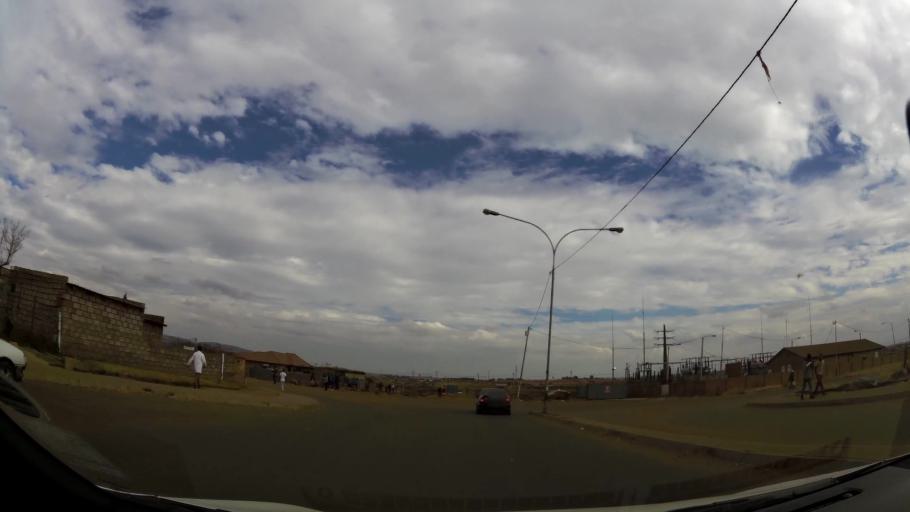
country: ZA
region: Gauteng
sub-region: Ekurhuleni Metropolitan Municipality
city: Germiston
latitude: -26.4092
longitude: 28.1525
